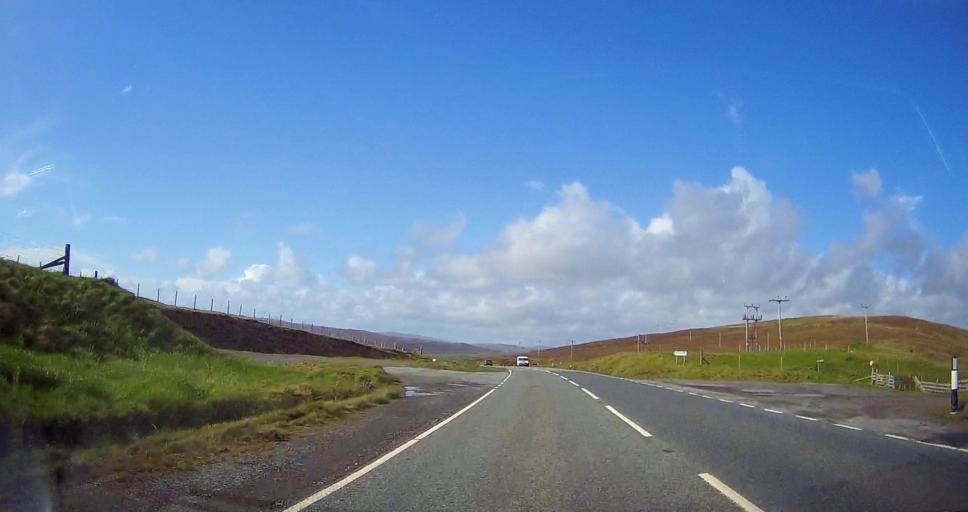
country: GB
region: Scotland
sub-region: Shetland Islands
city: Lerwick
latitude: 60.1752
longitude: -1.2229
